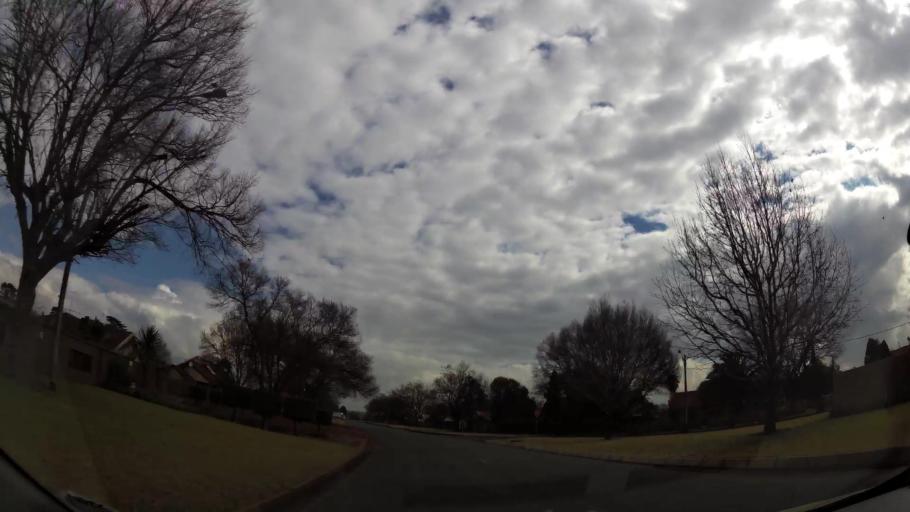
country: ZA
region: Gauteng
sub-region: Sedibeng District Municipality
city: Vereeniging
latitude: -26.6400
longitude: 27.9780
